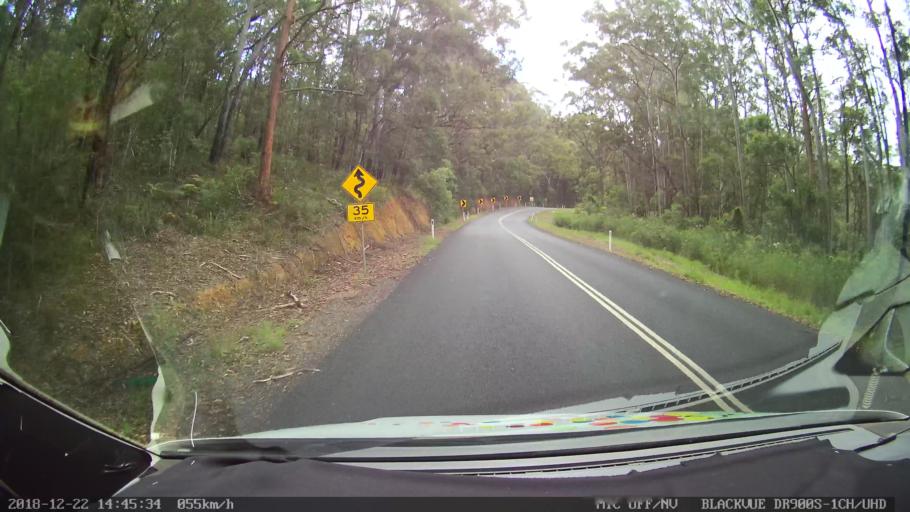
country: AU
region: New South Wales
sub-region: Bellingen
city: Dorrigo
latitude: -30.1708
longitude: 152.5681
